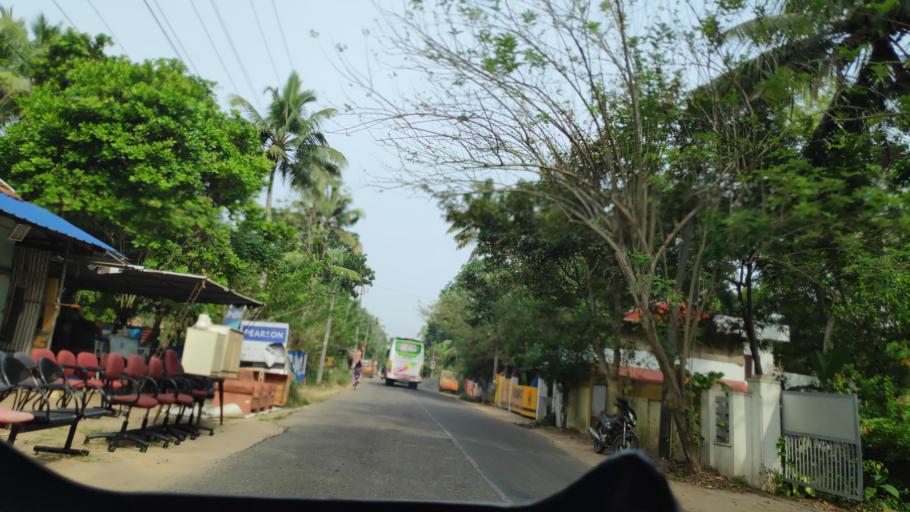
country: IN
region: Kerala
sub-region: Alappuzha
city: Kutiatodu
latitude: 9.8117
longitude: 76.3526
